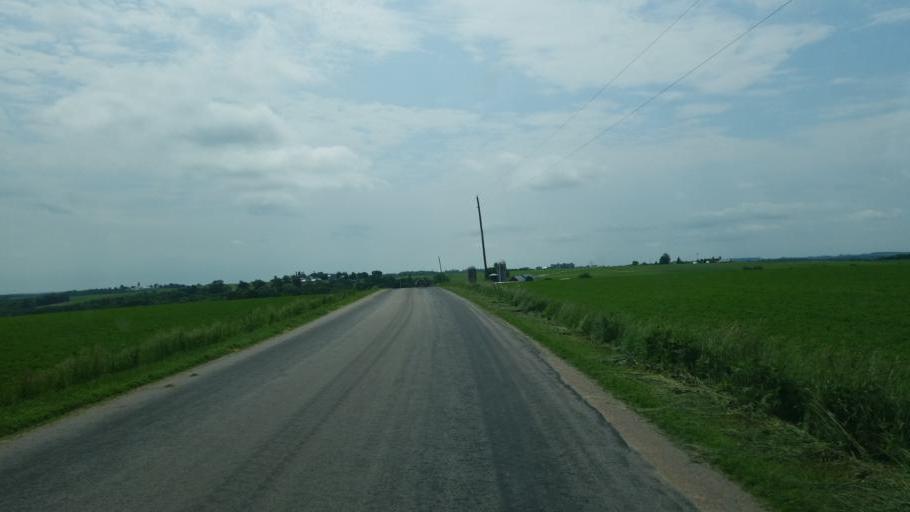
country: US
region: Wisconsin
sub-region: Monroe County
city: Cashton
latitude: 43.7806
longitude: -90.6694
